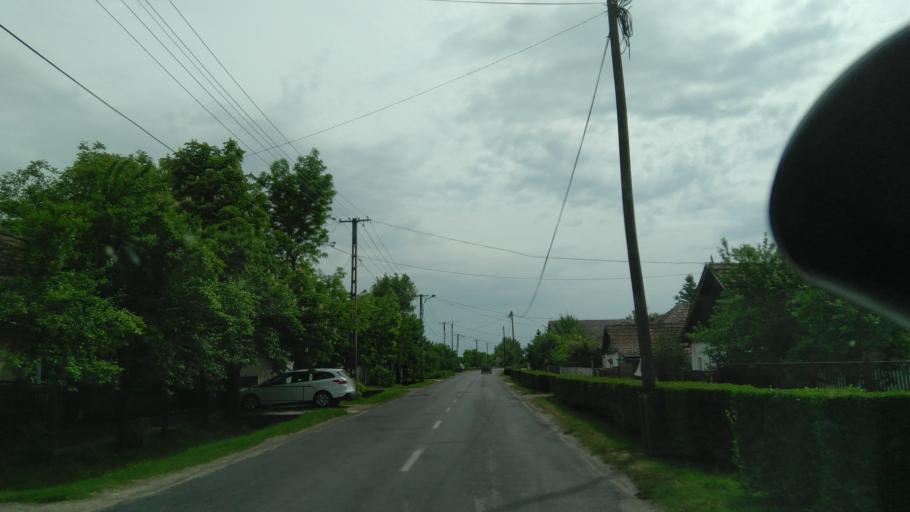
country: HU
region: Bekes
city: Sarkad
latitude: 46.8003
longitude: 21.3845
